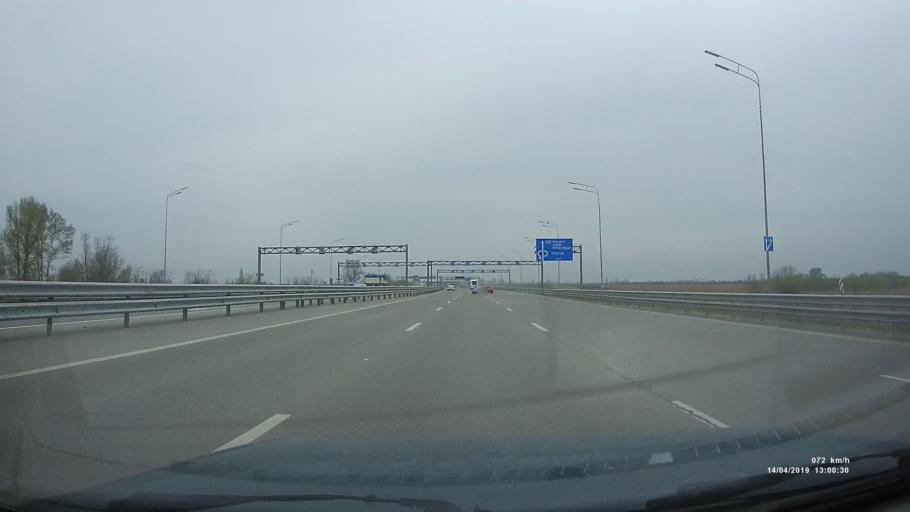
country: RU
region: Rostov
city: Rostov-na-Donu
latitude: 47.1978
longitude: 39.7302
